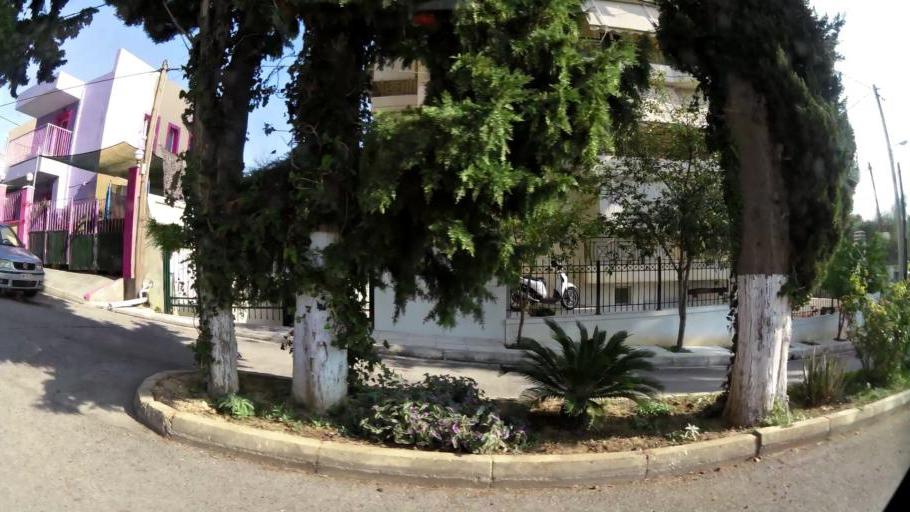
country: GR
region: Attica
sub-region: Nomarchia Athinas
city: Nea Filadelfeia
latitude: 38.0543
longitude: 23.7406
